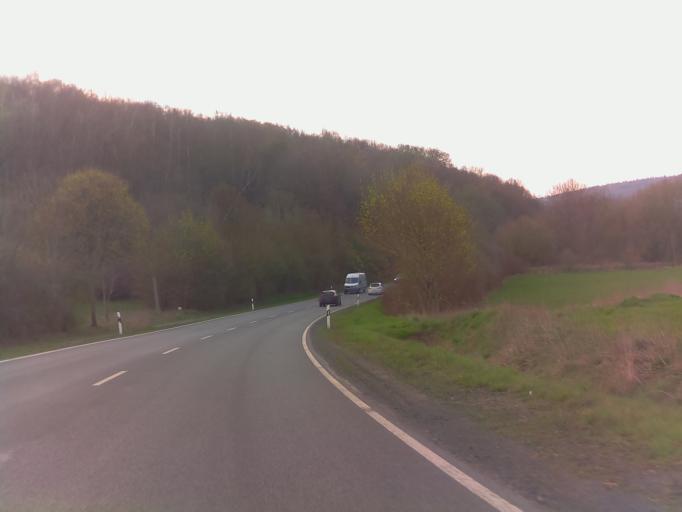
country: DE
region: Hesse
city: Philippsthal
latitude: 50.8324
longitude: 10.0109
